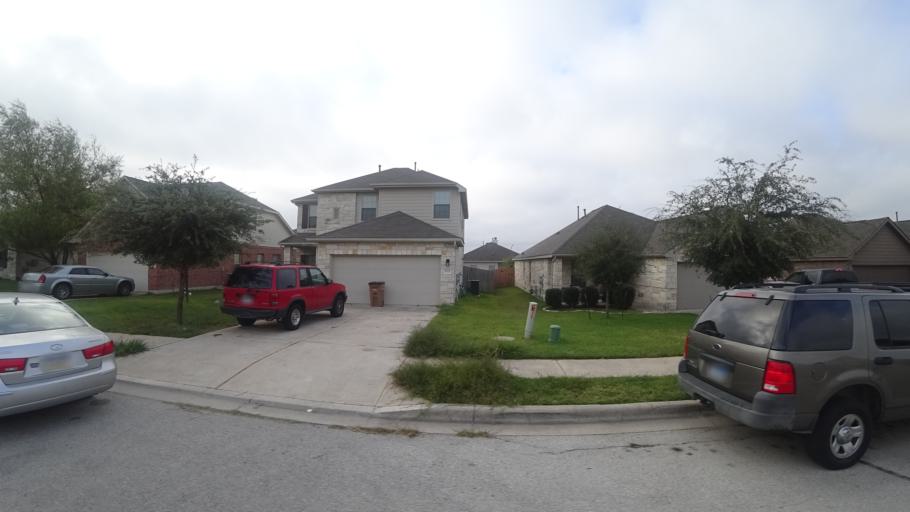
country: US
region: Texas
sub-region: Travis County
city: Pflugerville
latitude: 30.3615
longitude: -97.6425
